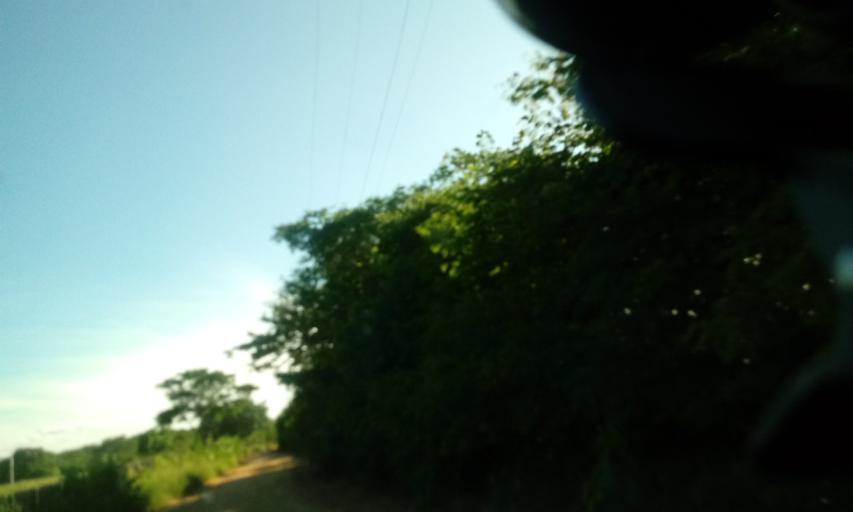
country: BR
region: Bahia
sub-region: Riacho De Santana
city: Riacho de Santana
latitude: -13.8034
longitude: -42.7542
